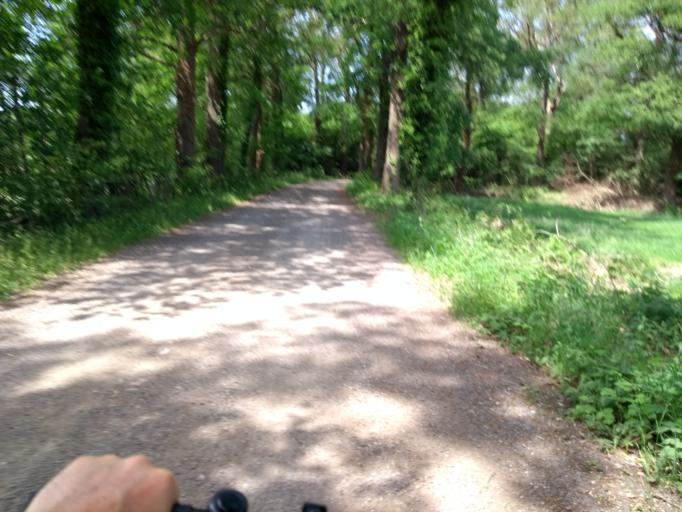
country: NL
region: Overijssel
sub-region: Gemeente Almelo
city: Almelo
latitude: 52.3617
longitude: 6.7002
